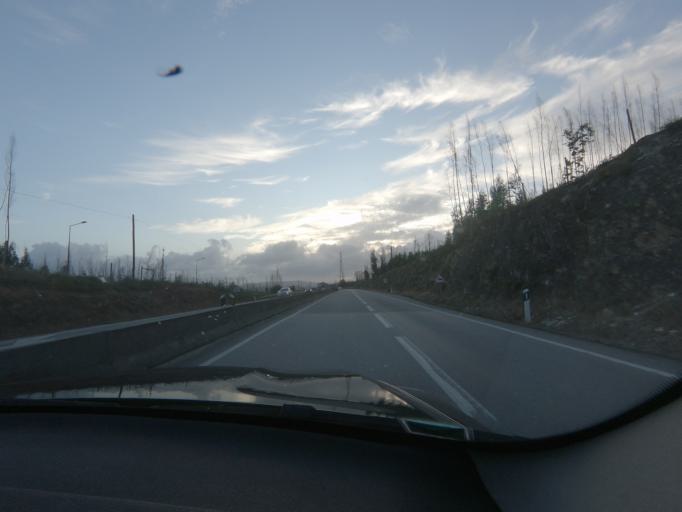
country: PT
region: Viseu
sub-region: Mortagua
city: Mortagua
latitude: 40.3534
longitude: -8.1961
